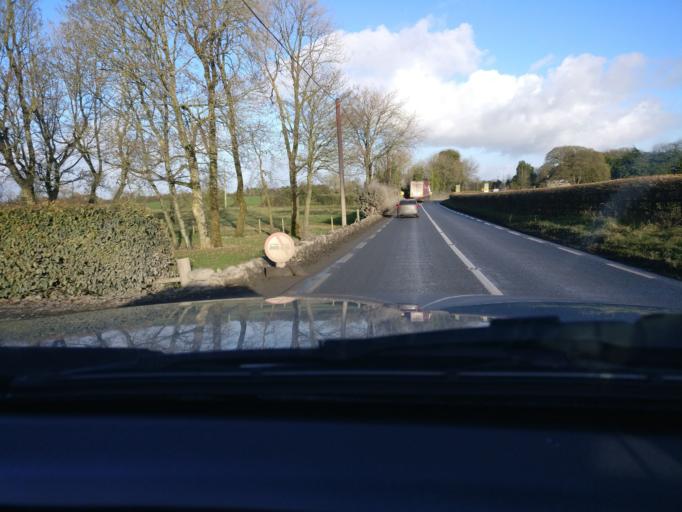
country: IE
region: Leinster
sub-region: An Iarmhi
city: Rathwire
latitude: 53.5794
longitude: -7.1545
